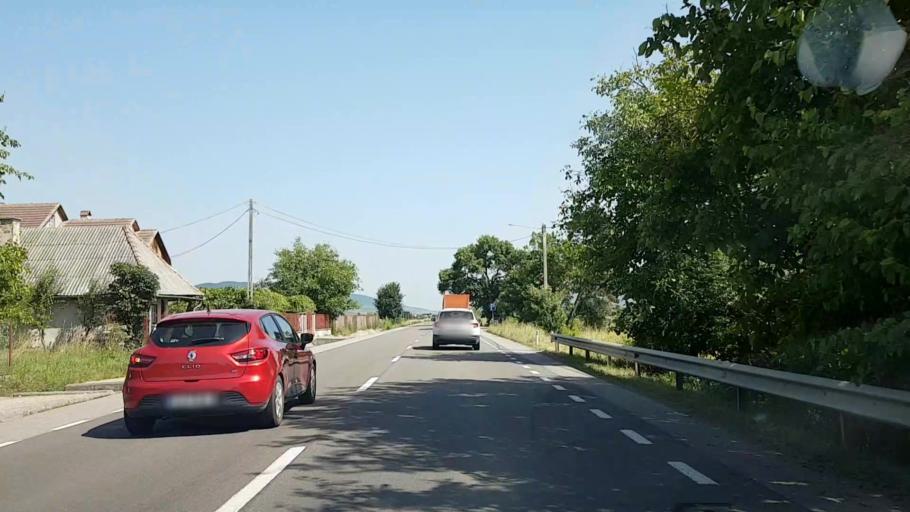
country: RO
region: Bistrita-Nasaud
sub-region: Comuna Sieu-Odorhei
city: Sieu-Odorhei
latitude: 47.1283
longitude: 24.3156
